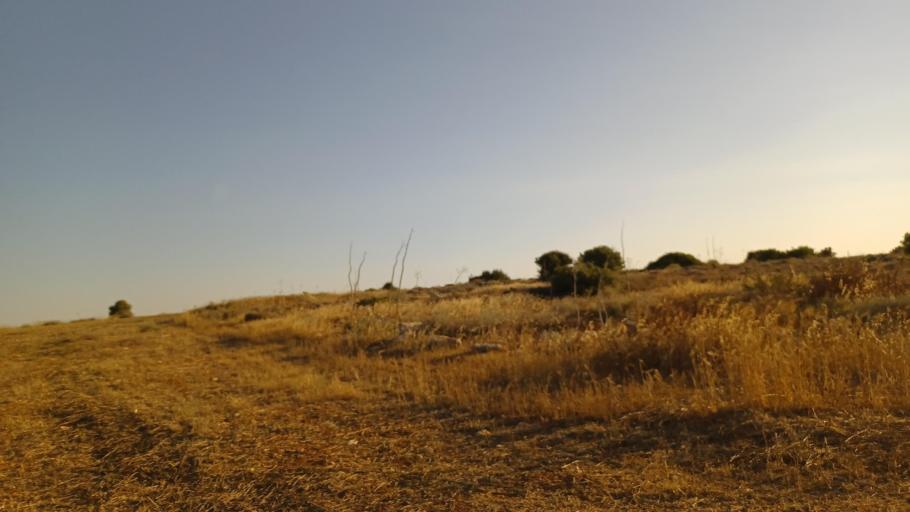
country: CY
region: Larnaka
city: Pyla
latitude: 34.9939
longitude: 33.7091
